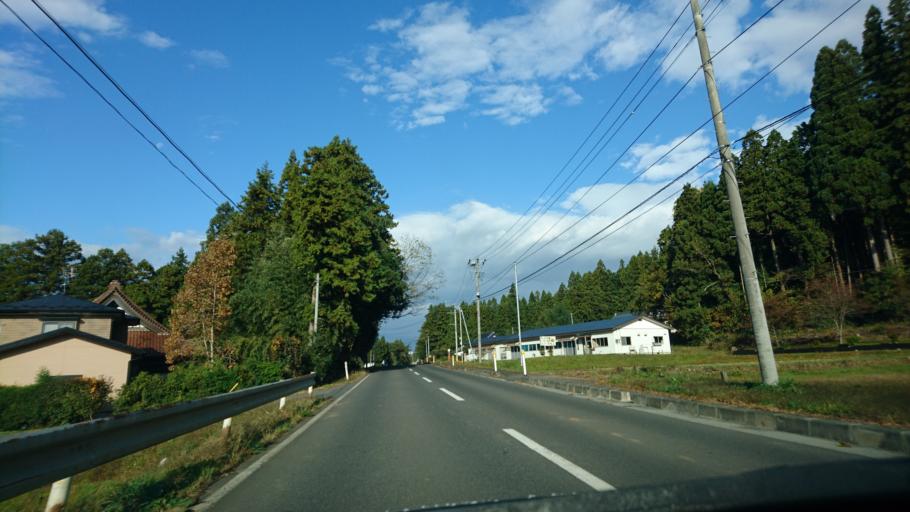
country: JP
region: Iwate
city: Mizusawa
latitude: 39.0348
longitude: 141.0751
